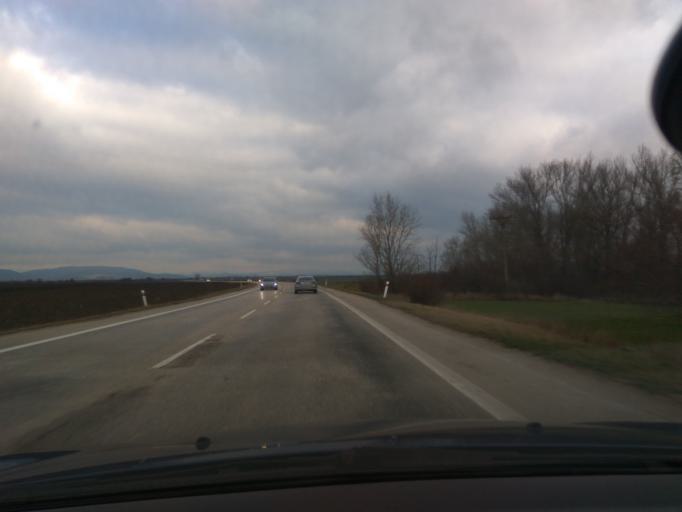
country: SK
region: Trnavsky
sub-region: Okres Trnava
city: Piestany
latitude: 48.6311
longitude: 17.8394
